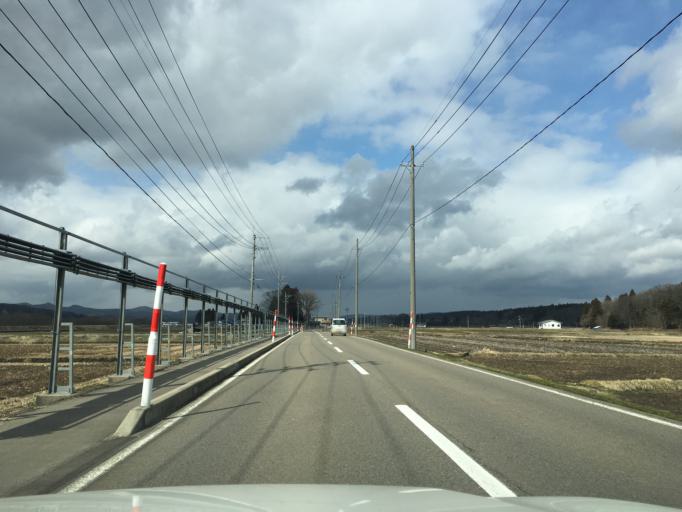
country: JP
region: Akita
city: Takanosu
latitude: 40.1320
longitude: 140.3584
